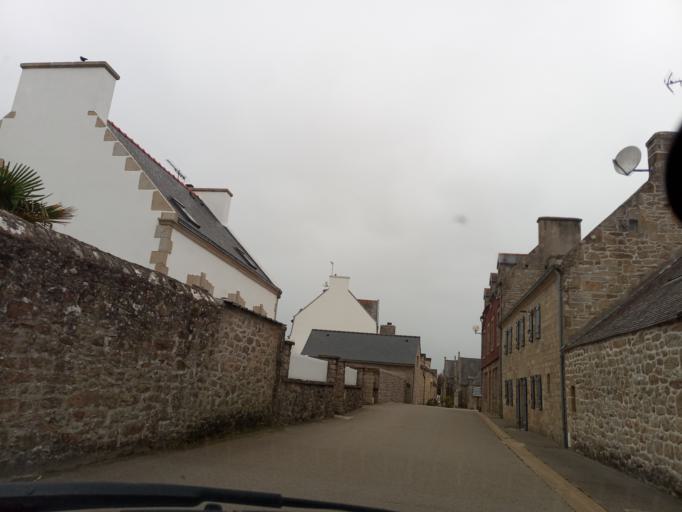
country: FR
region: Brittany
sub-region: Departement du Finistere
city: Esquibien
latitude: 48.0240
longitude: -4.5613
